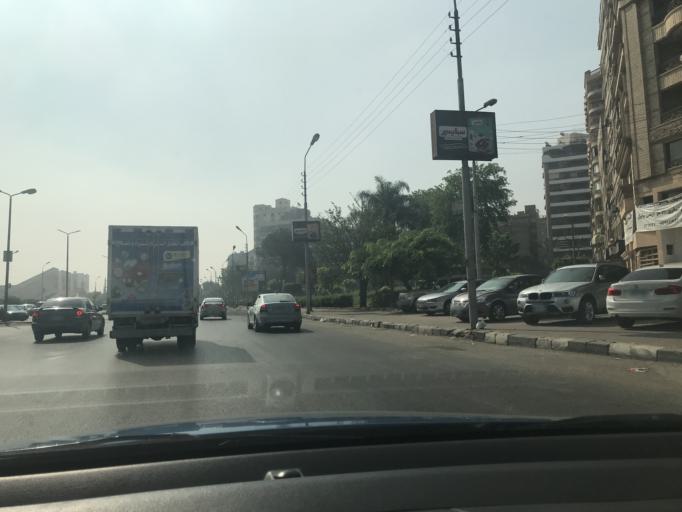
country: EG
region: Muhafazat al Qalyubiyah
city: Al Khankah
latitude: 30.1180
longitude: 31.3583
